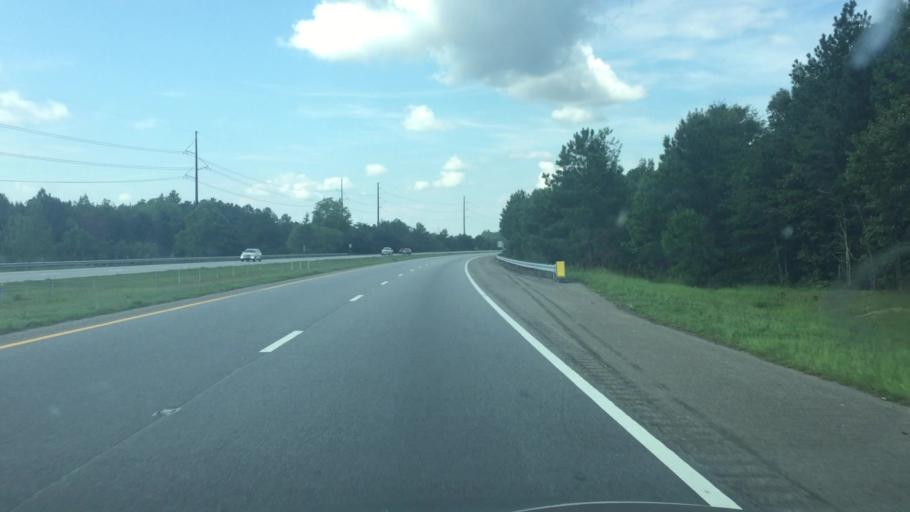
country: US
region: North Carolina
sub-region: Richmond County
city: Hamlet
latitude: 34.8580
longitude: -79.6836
